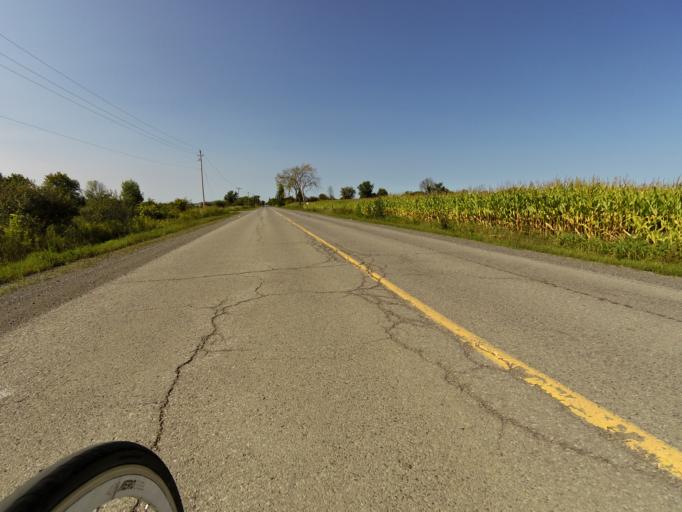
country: CA
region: Ontario
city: Carleton Place
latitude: 45.3329
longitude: -76.0912
